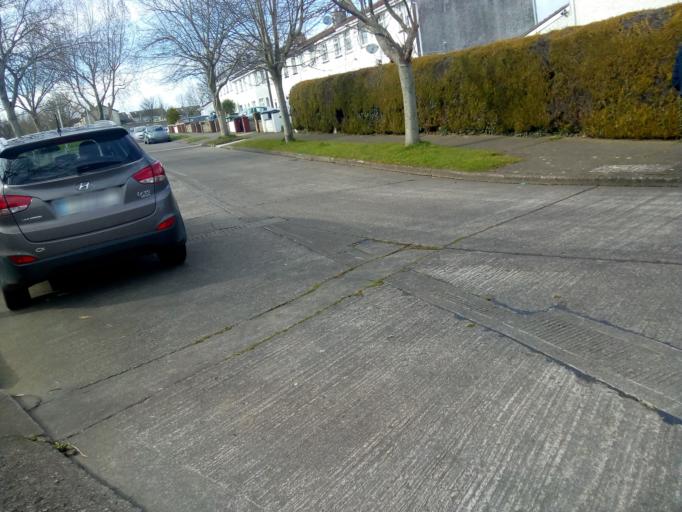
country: IE
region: Leinster
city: Balbriggan
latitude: 53.6064
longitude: -6.1862
